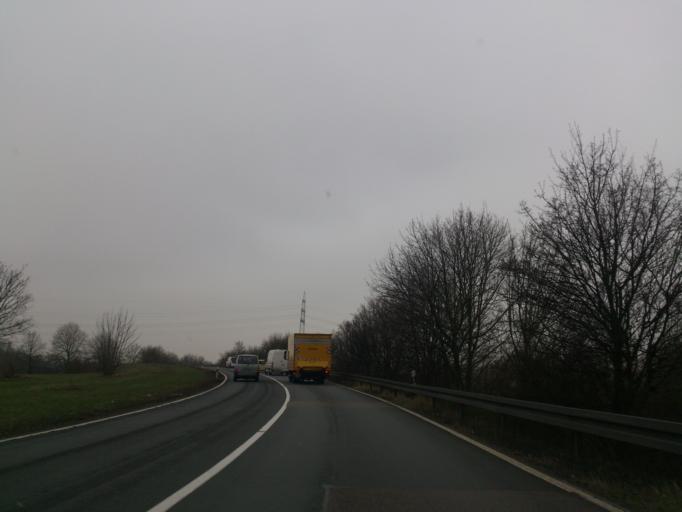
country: DE
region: North Rhine-Westphalia
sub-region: Regierungsbezirk Dusseldorf
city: Dusseldorf
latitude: 51.1584
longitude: 6.7575
